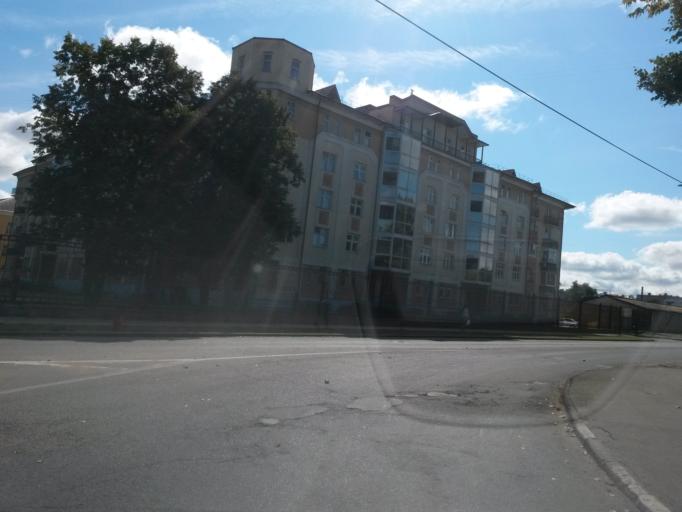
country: RU
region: Jaroslavl
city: Yaroslavl
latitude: 57.6096
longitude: 39.8738
